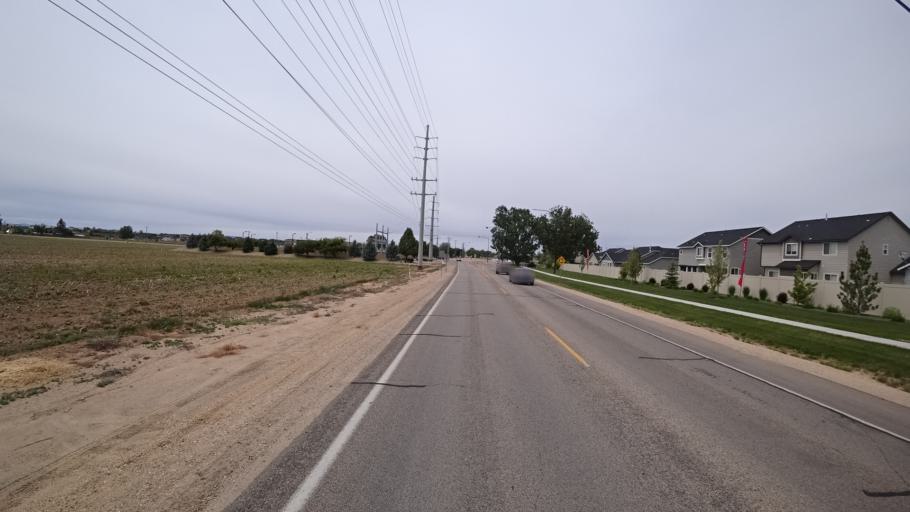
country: US
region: Idaho
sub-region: Ada County
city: Meridian
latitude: 43.5612
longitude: -116.3520
